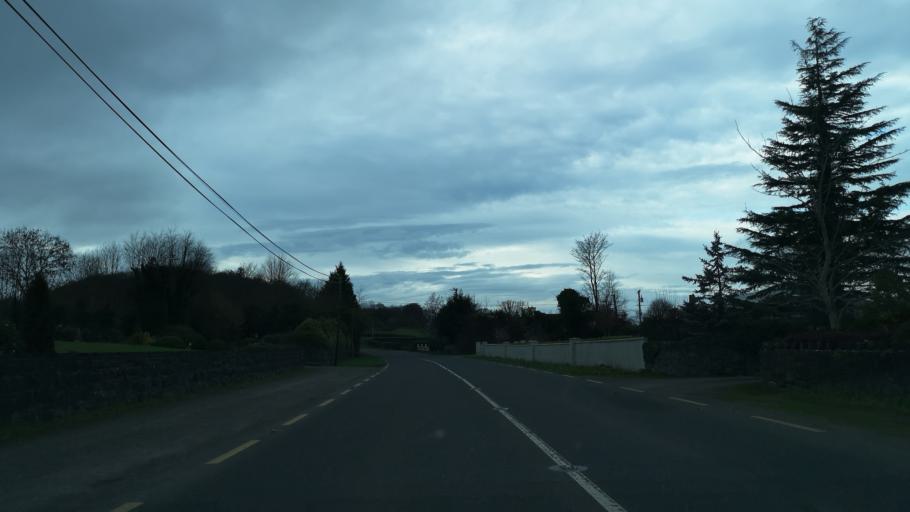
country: IE
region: Connaught
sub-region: County Galway
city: Portumna
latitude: 53.1684
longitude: -8.3079
